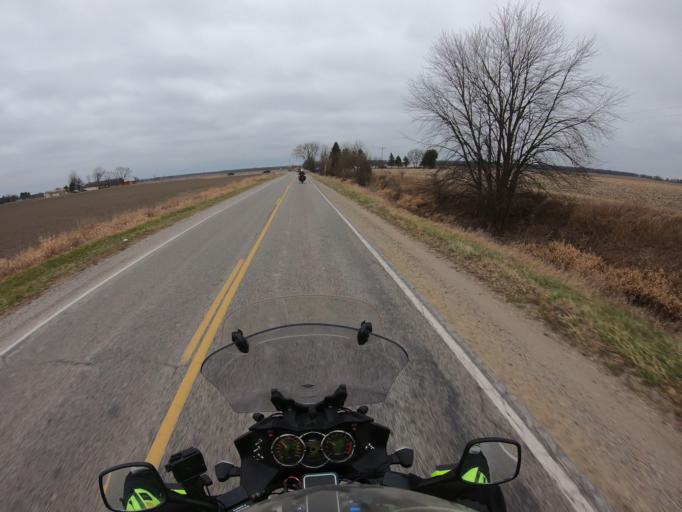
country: US
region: Michigan
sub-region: Saginaw County
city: Saint Charles
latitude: 43.2649
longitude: -84.1098
